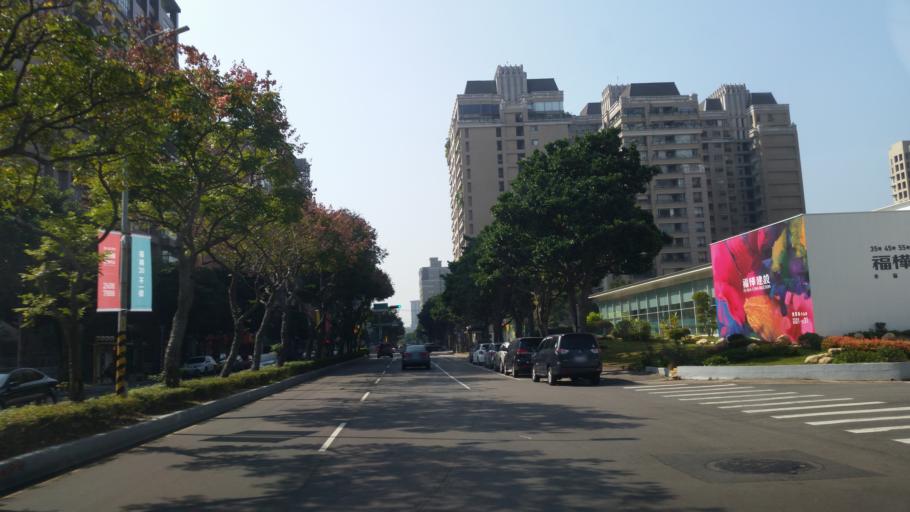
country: TW
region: Taiwan
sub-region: Taoyuan
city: Taoyuan
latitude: 25.0743
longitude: 121.3716
